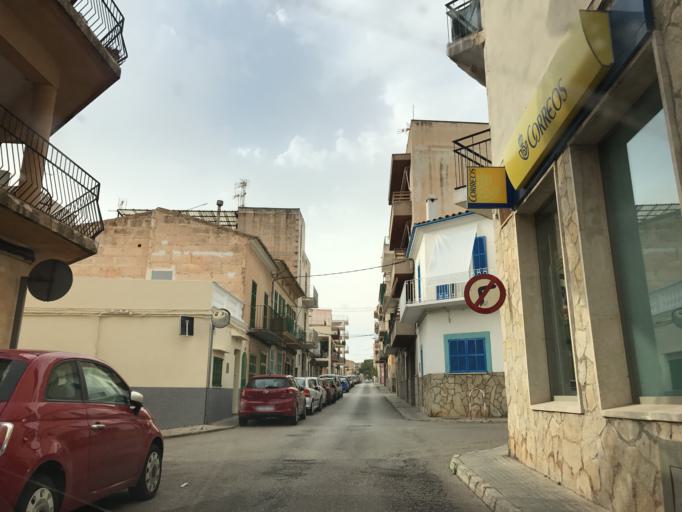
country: ES
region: Balearic Islands
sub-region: Illes Balears
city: Son Servera
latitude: 39.5418
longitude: 3.3330
